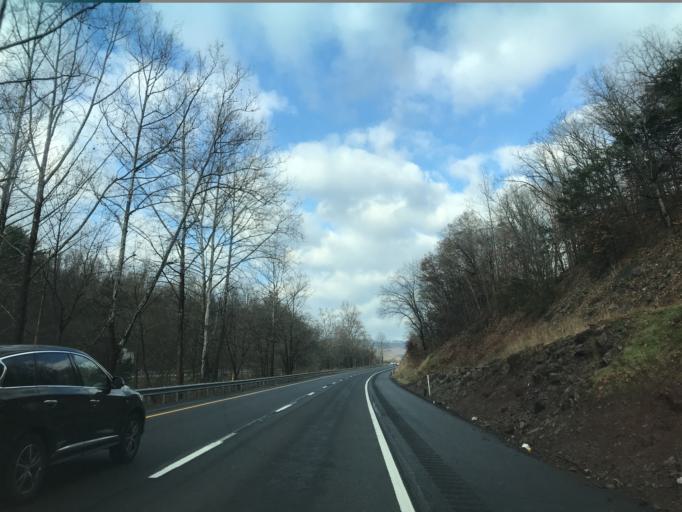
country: US
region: Maryland
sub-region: Washington County
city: Hancock
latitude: 39.7999
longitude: -78.2510
